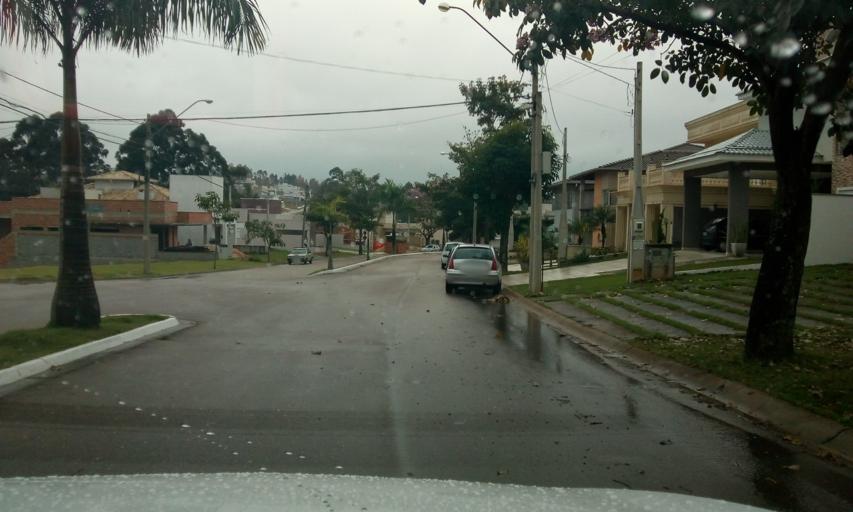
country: BR
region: Sao Paulo
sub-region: Itupeva
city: Itupeva
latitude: -23.1383
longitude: -47.0522
